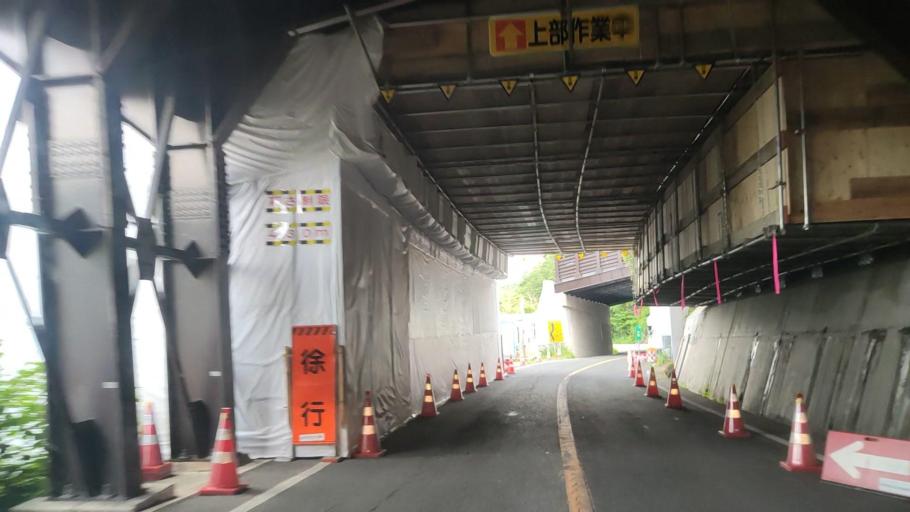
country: JP
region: Tottori
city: Yonago
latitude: 35.3647
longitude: 133.5213
